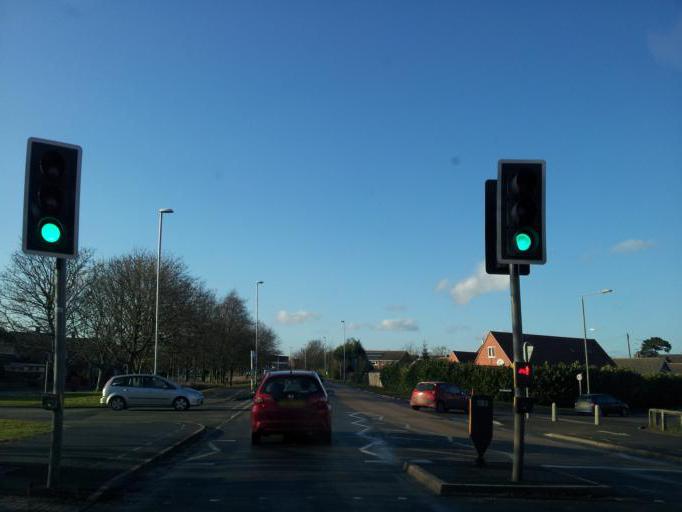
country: GB
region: England
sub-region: Nottinghamshire
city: Newark on Trent
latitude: 53.0515
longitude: -0.7798
